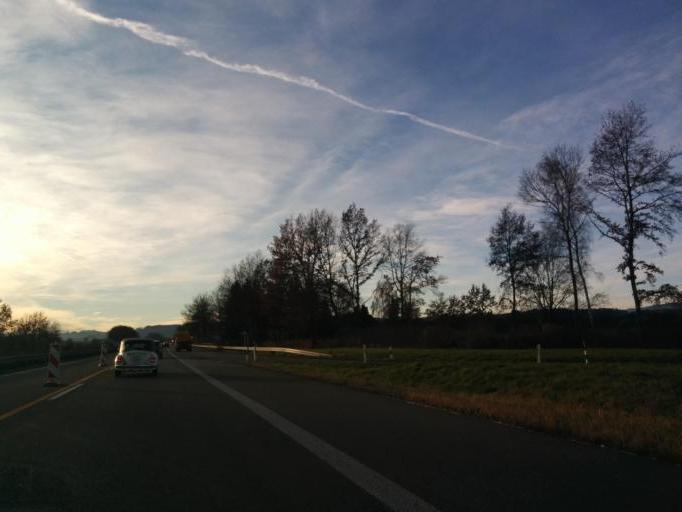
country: DE
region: Bavaria
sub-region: Swabia
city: Durach
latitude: 47.6836
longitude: 10.3309
